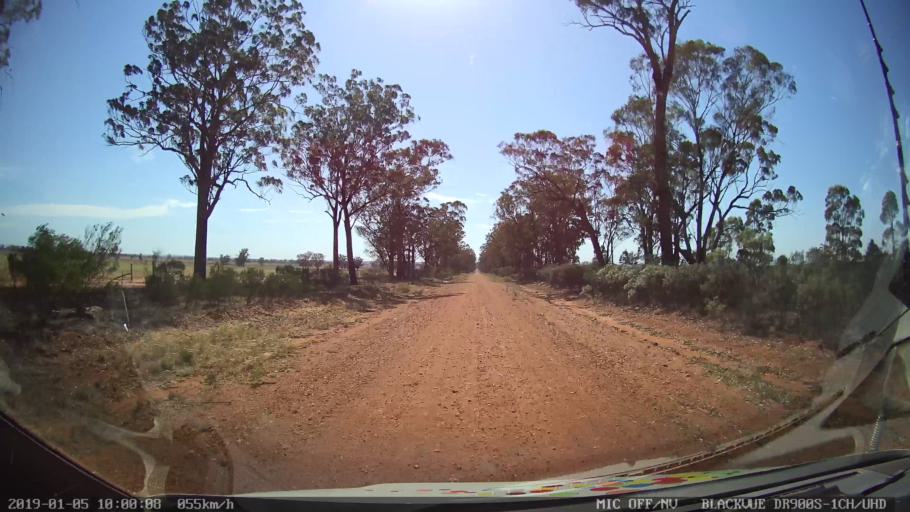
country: AU
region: New South Wales
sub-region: Gilgandra
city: Gilgandra
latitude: -31.6683
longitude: 148.8241
